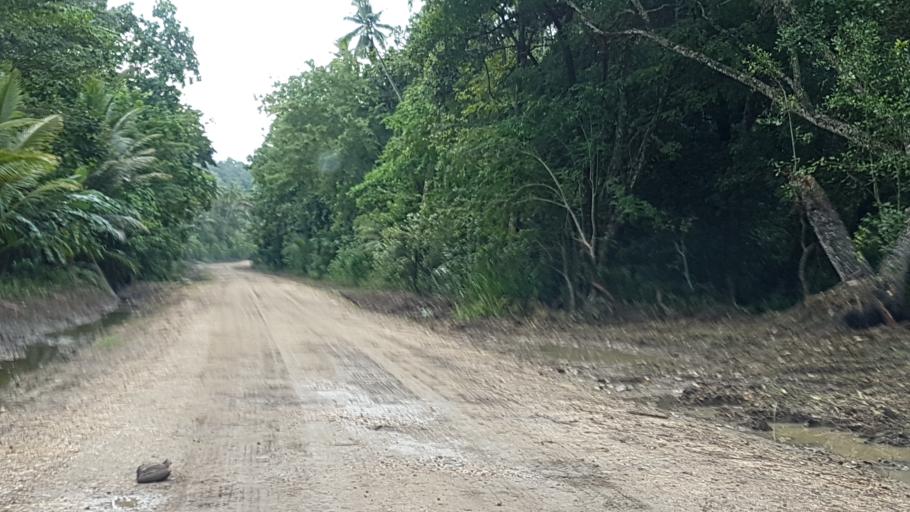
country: PG
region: Milne Bay
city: Alotau
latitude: -10.2956
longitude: 150.7422
